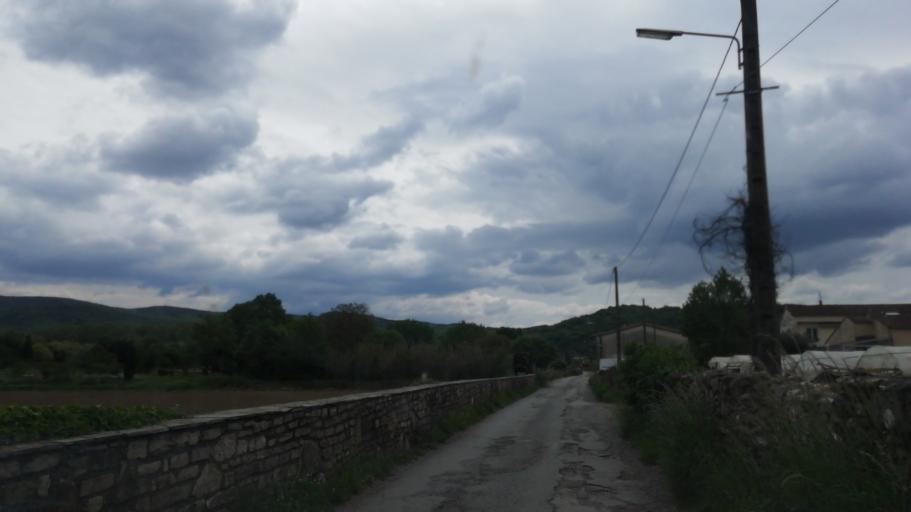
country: FR
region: Languedoc-Roussillon
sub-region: Departement de l'Herault
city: Cazilhac
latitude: 43.9262
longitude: 3.7057
